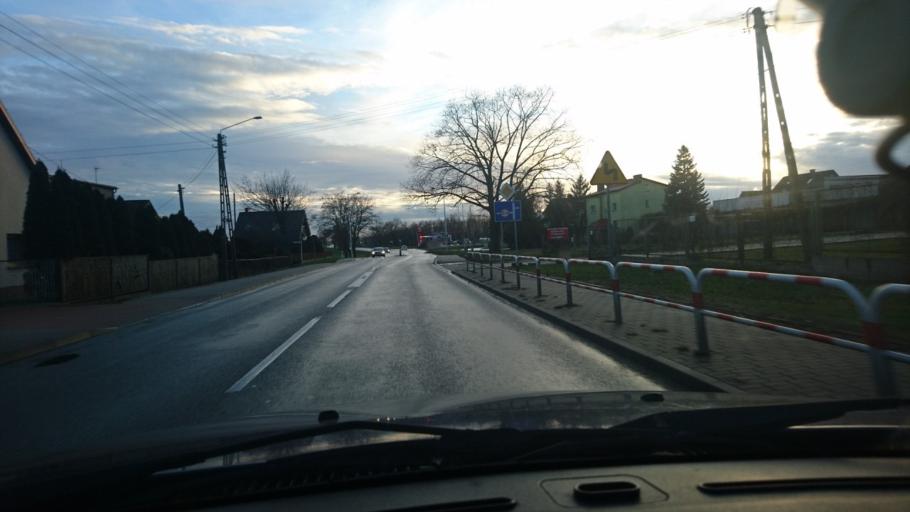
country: PL
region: Opole Voivodeship
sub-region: Powiat kluczborski
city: Byczyna
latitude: 51.1103
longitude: 18.2075
